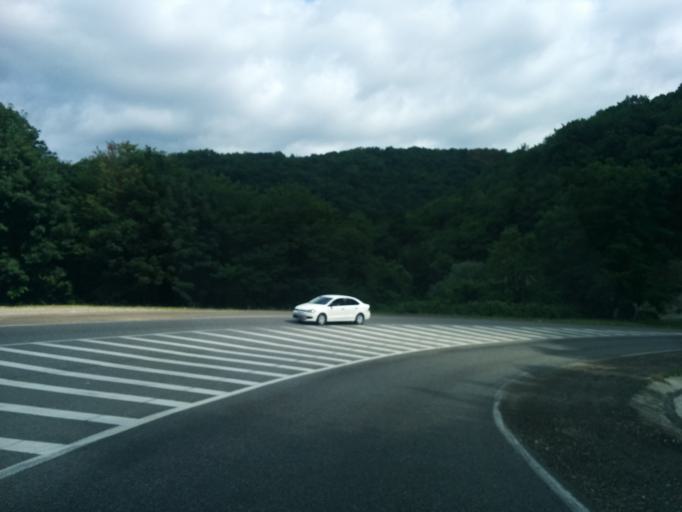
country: RU
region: Krasnodarskiy
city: Agoy
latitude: 44.1422
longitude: 39.0556
